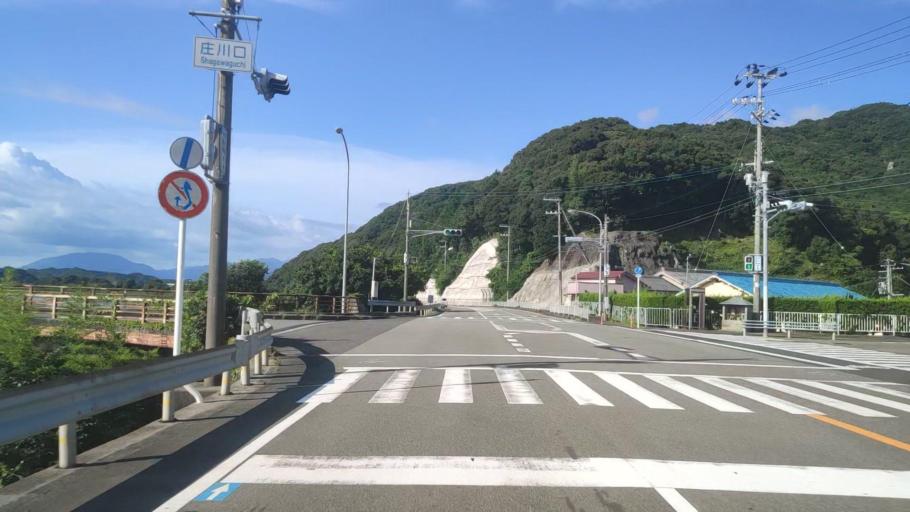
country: JP
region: Wakayama
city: Tanabe
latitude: 33.6654
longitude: 135.4066
